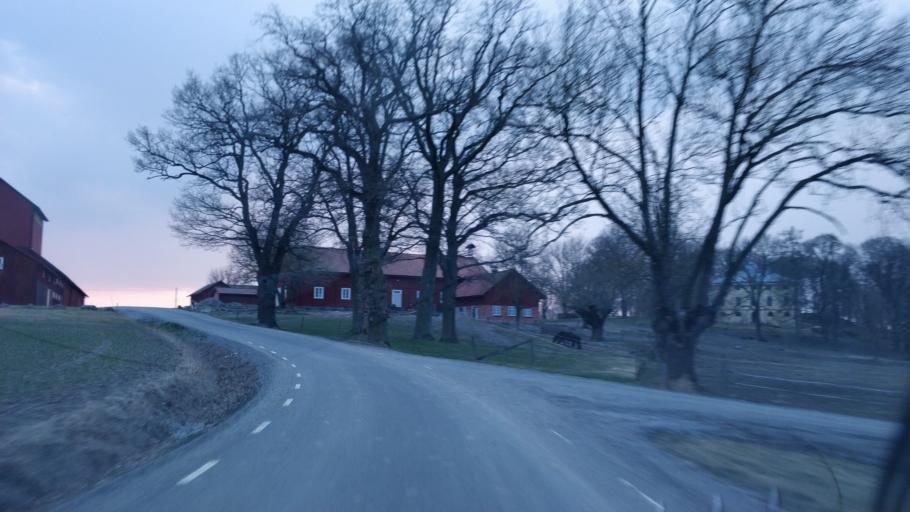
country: SE
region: Uppsala
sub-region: Enkopings Kommun
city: Orsundsbro
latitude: 59.7400
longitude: 17.1827
